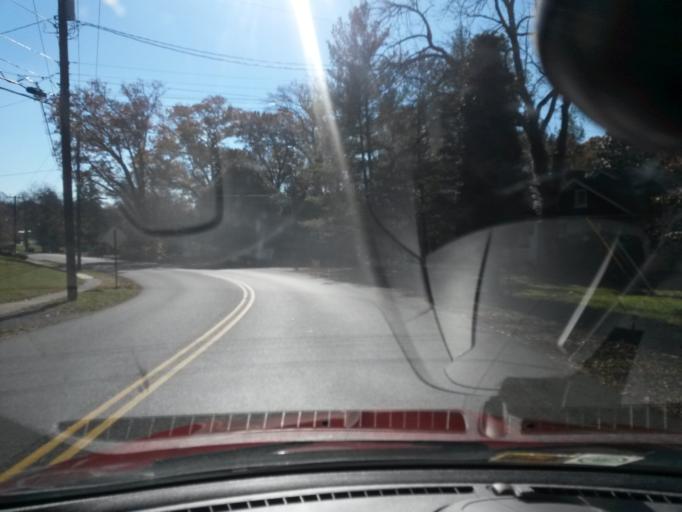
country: US
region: Virginia
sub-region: City of Bedford
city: Bedford
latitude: 37.3451
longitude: -79.5278
